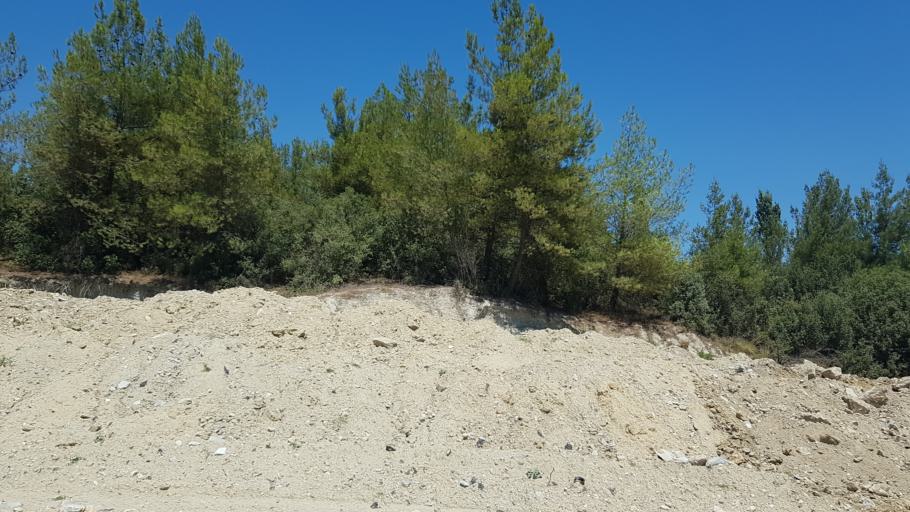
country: TR
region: Mugla
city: Yatagan
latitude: 37.3183
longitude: 28.0861
